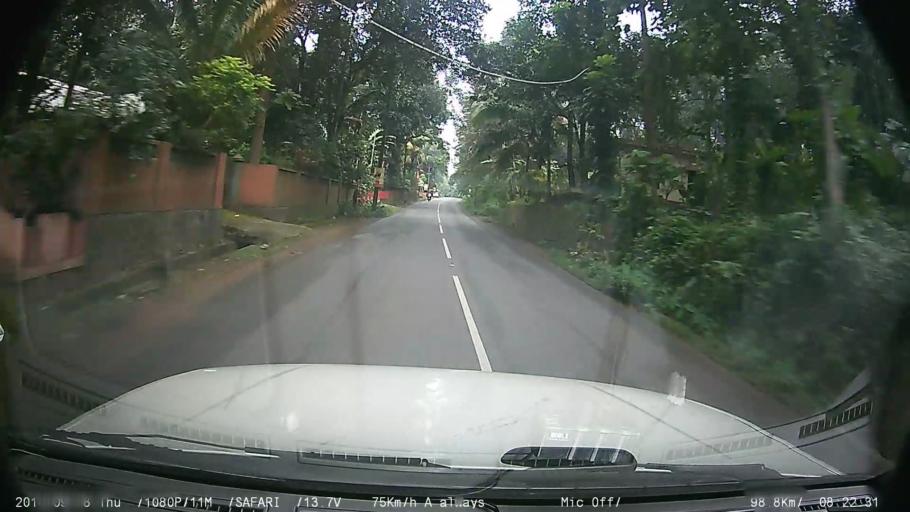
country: IN
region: Kerala
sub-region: Kottayam
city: Palackattumala
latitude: 9.6624
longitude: 76.6103
